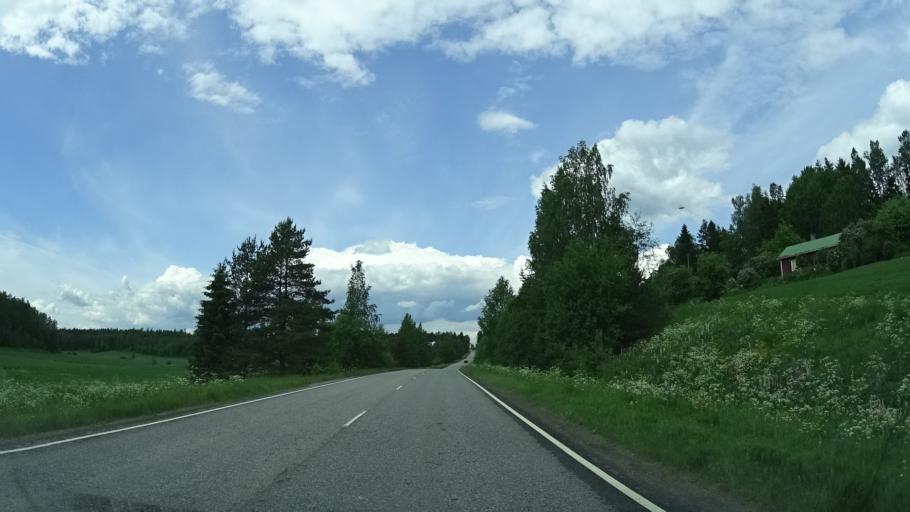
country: FI
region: Uusimaa
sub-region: Helsinki
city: Espoo
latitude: 60.1944
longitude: 24.5630
